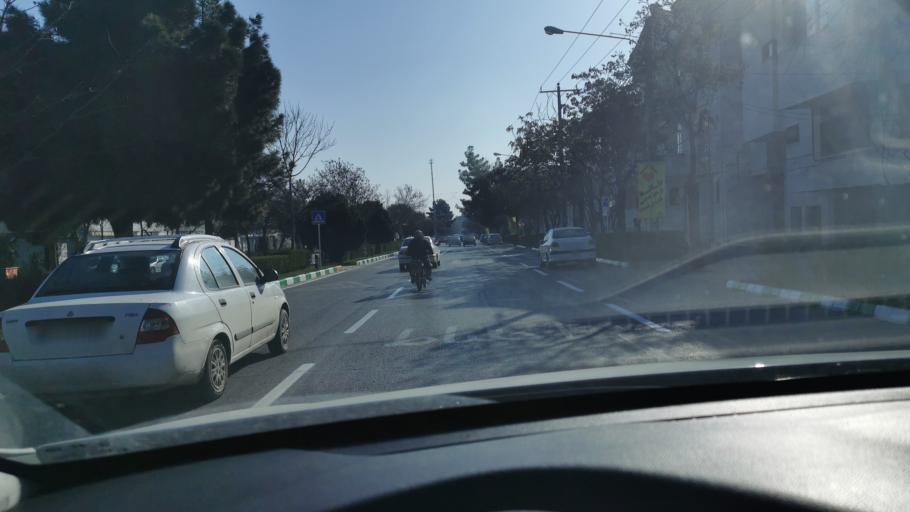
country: IR
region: Razavi Khorasan
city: Mashhad
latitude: 36.2927
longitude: 59.5629
